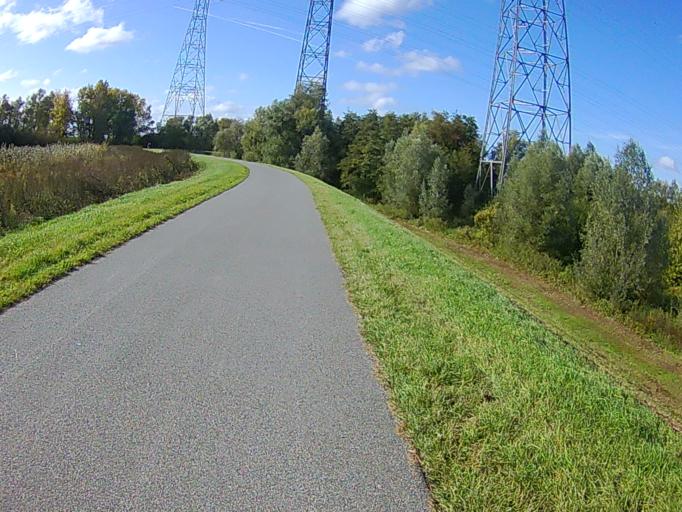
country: BE
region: Flanders
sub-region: Provincie Antwerpen
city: Niel
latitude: 51.1287
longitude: 4.3079
